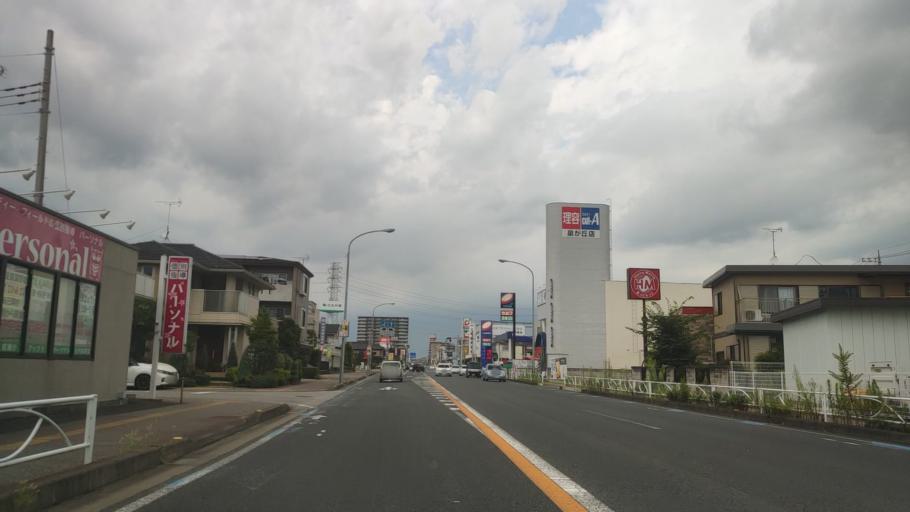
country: JP
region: Tochigi
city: Utsunomiya-shi
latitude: 36.5669
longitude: 139.9161
